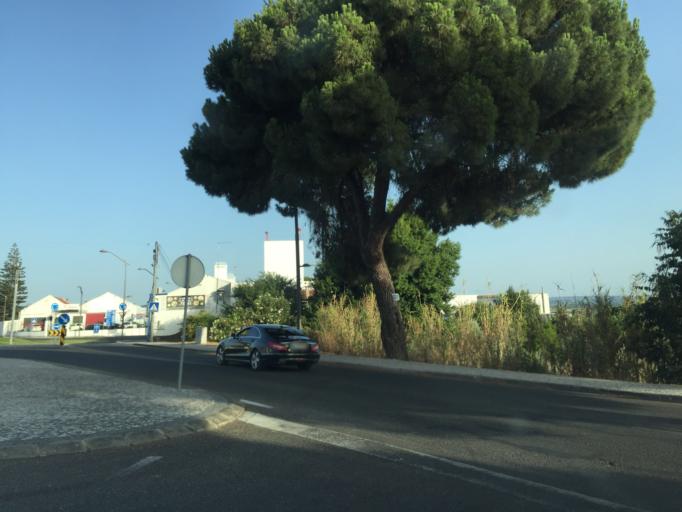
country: PT
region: Santarem
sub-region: Chamusca
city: Vila Nova da Barquinha
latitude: 39.4616
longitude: -8.4359
